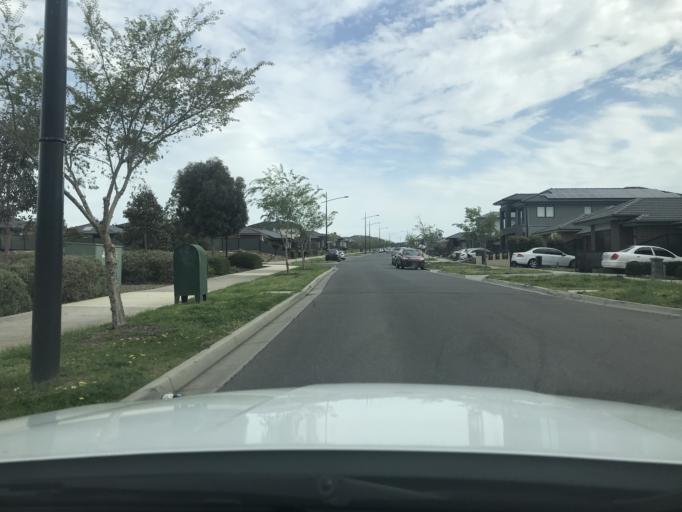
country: AU
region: Victoria
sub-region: Hume
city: Roxburgh Park
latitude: -37.5964
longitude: 144.8978
